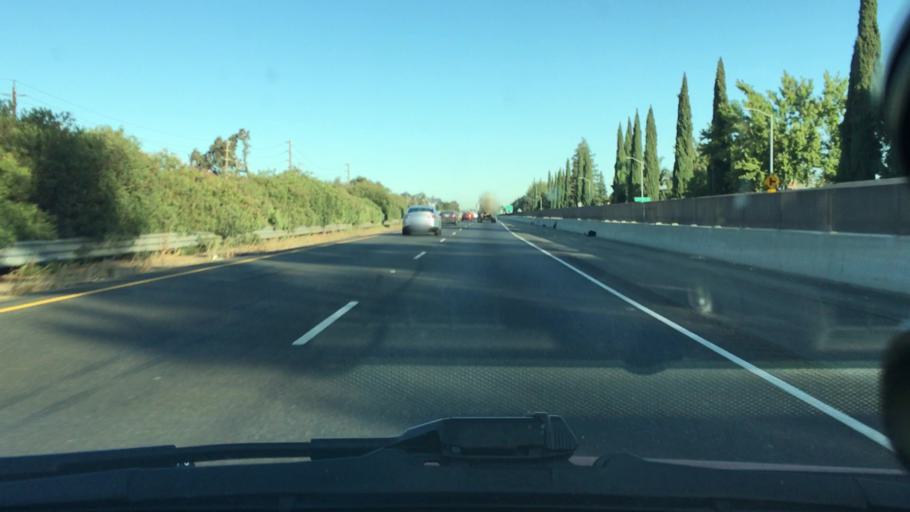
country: US
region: California
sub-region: Sacramento County
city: Elk Grove
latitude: 38.3970
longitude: -121.3806
